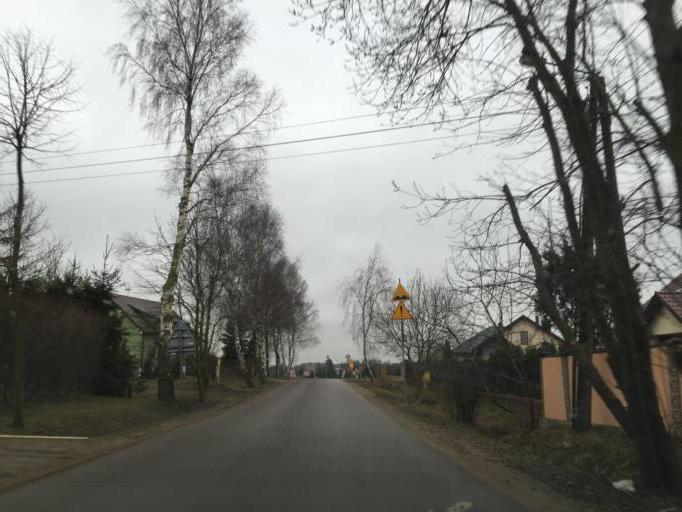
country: PL
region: Pomeranian Voivodeship
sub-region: Powiat kartuski
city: Banino
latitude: 54.3939
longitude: 18.4316
